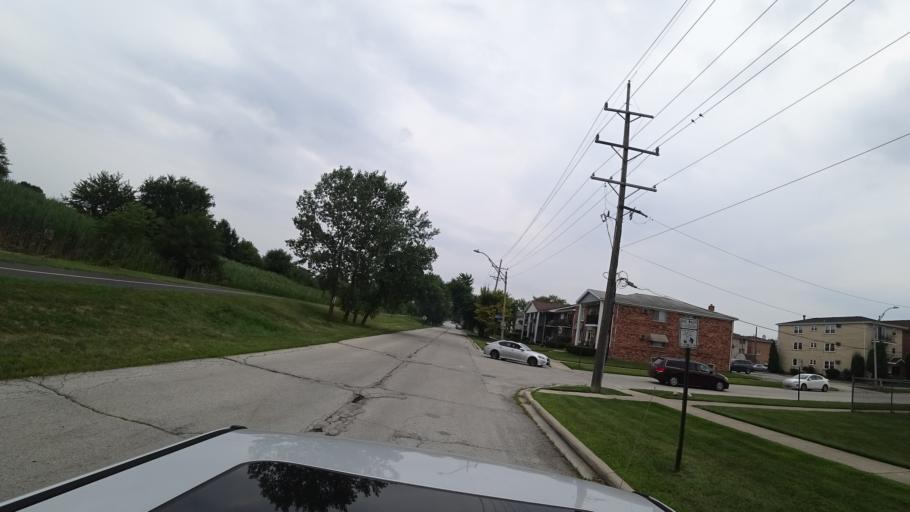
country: US
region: Illinois
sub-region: Cook County
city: Chicago Ridge
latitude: 41.7050
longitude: -87.7723
